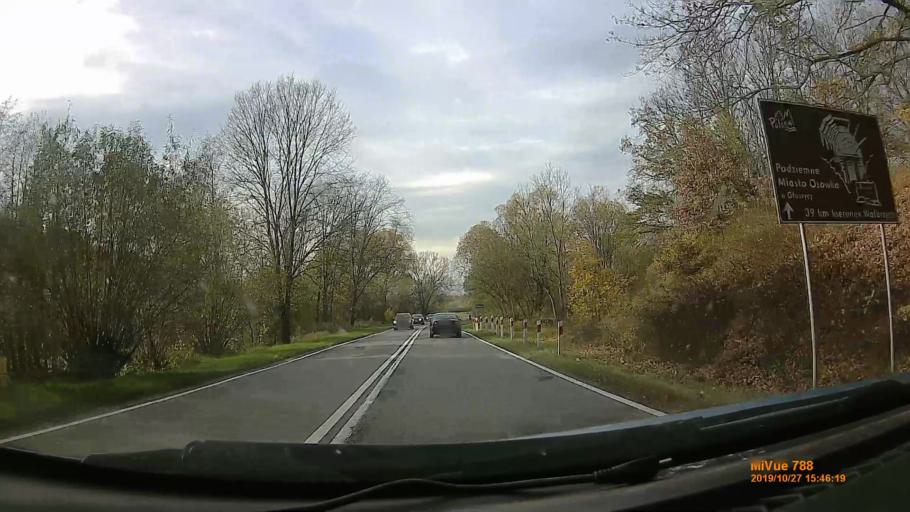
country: PL
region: Lower Silesian Voivodeship
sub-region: Powiat klodzki
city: Bozkow
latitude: 50.4811
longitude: 16.5860
